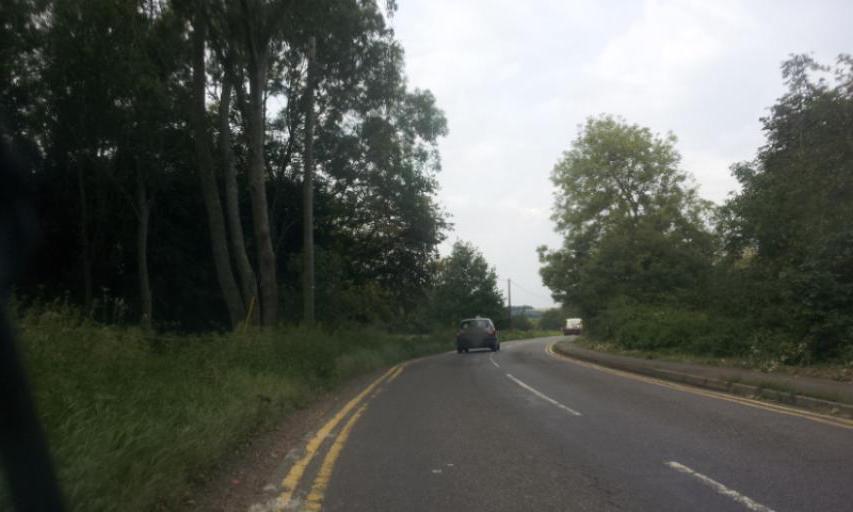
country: GB
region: England
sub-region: Kent
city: Yalding
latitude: 51.2184
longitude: 0.4205
